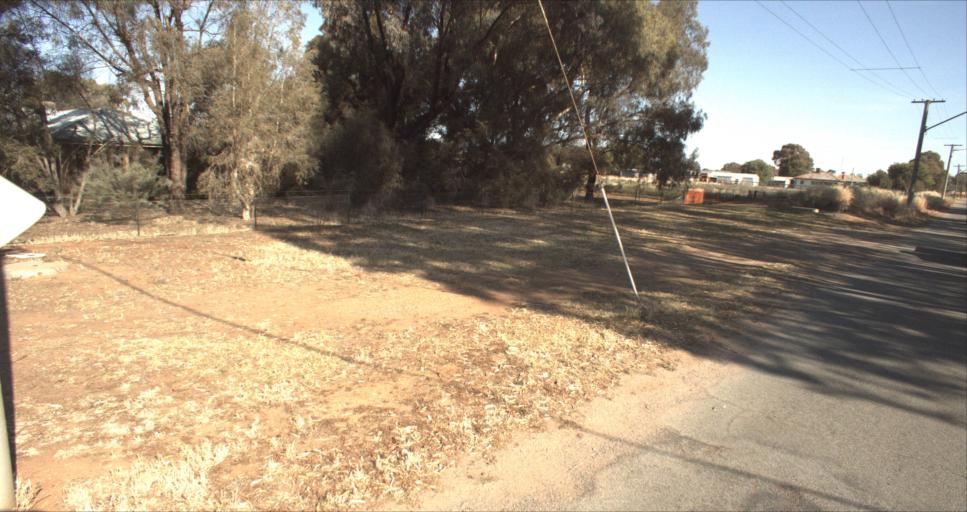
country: AU
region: New South Wales
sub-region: Leeton
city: Leeton
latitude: -34.5444
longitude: 146.4149
